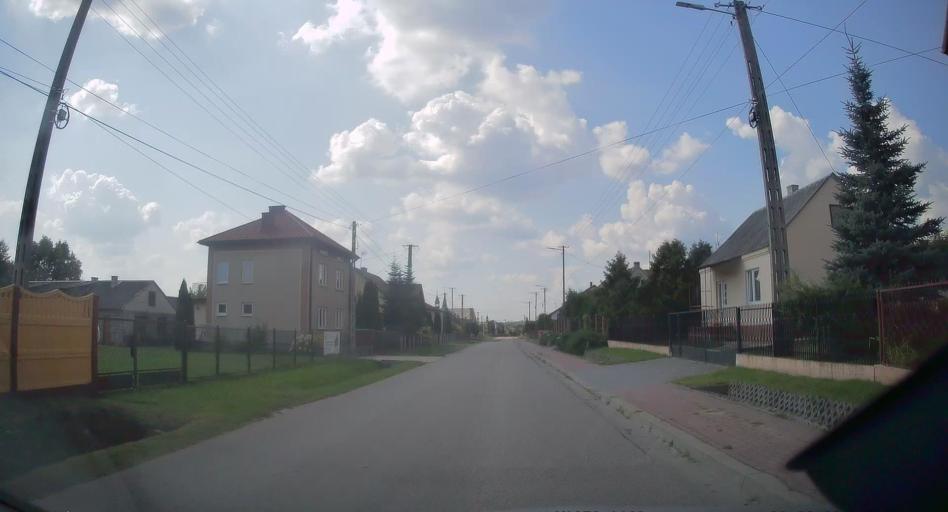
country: PL
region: Swietokrzyskie
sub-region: Powiat kielecki
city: Checiny
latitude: 50.8175
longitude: 20.4004
